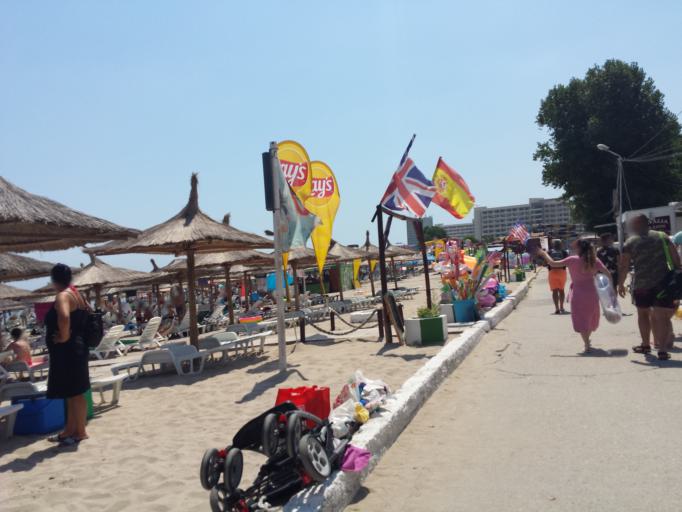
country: RO
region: Constanta
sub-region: Comuna Douazeci si Trei August
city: Douazeci si Trei August
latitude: 43.8609
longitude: 28.6062
